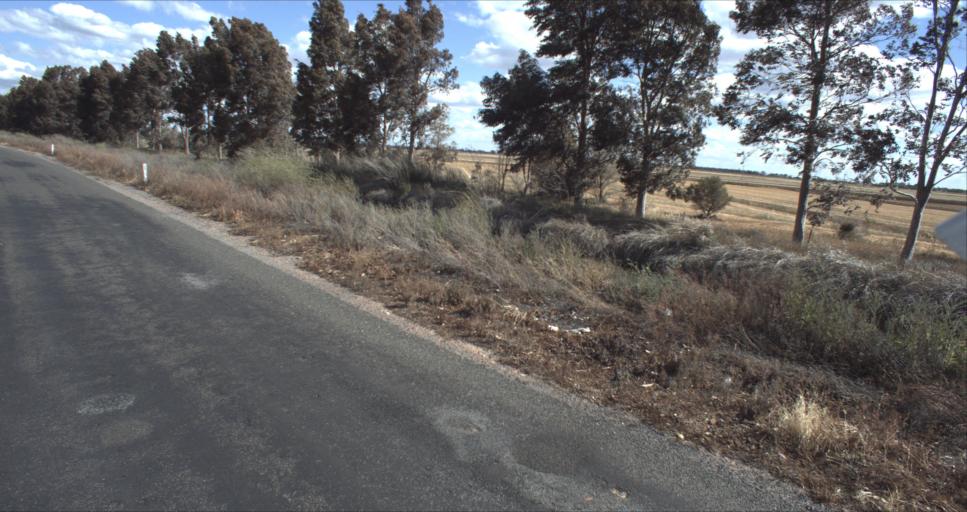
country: AU
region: New South Wales
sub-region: Griffith
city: Griffith
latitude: -34.4106
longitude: 146.2170
